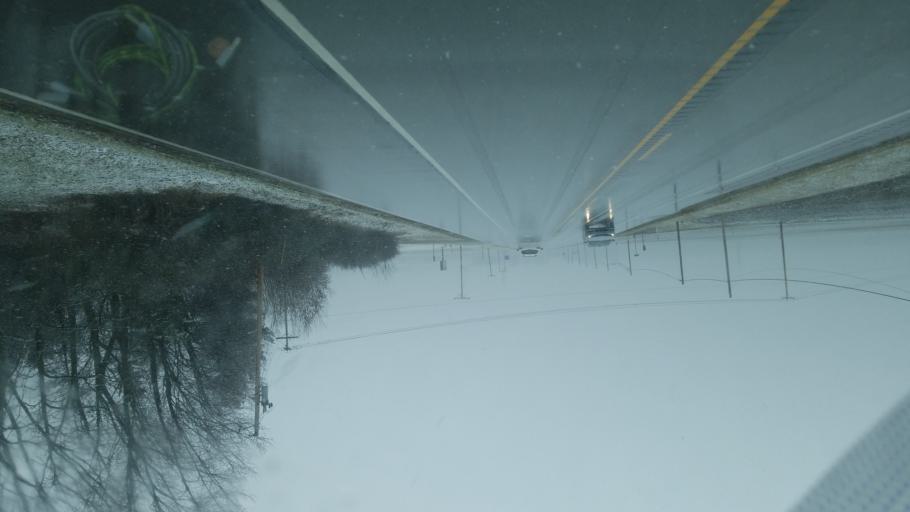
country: US
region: Indiana
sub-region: Grant County
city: Marion
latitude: 40.6264
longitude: -85.7020
